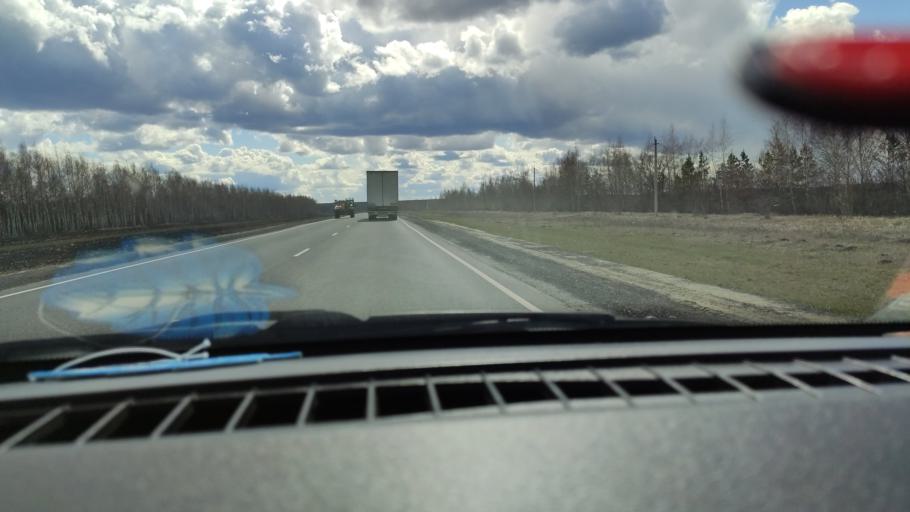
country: RU
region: Samara
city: Syzran'
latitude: 52.9870
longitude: 48.3182
